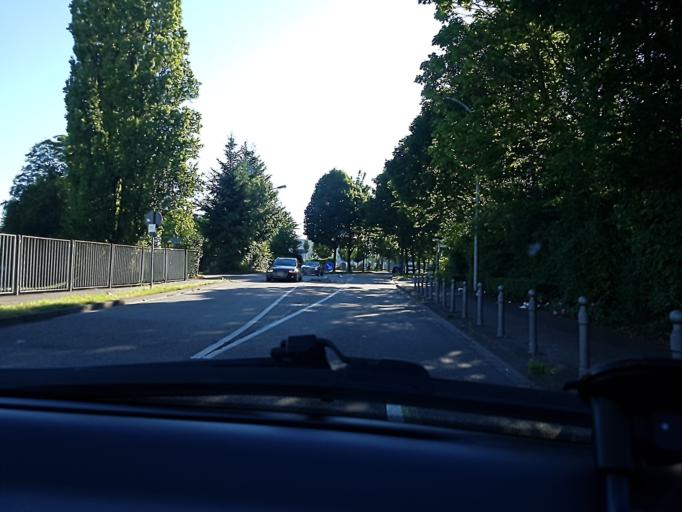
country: DE
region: Baden-Wuerttemberg
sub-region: Freiburg Region
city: Offenburg
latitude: 48.4810
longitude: 7.9540
